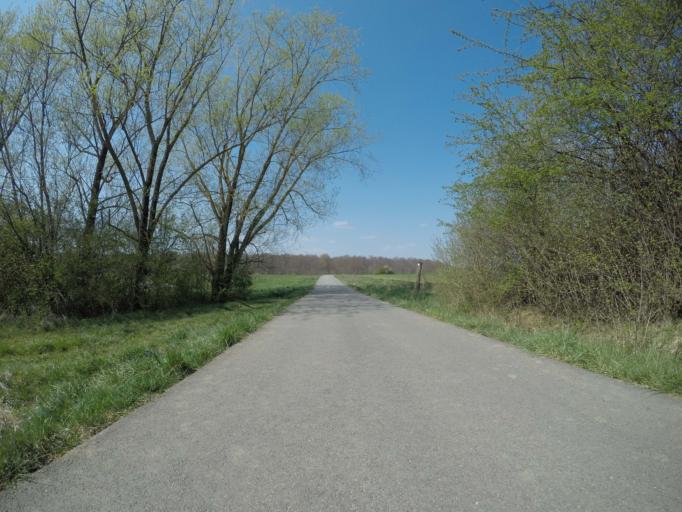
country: DE
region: Baden-Wuerttemberg
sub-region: Tuebingen Region
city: Gomaringen
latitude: 48.4583
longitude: 9.1452
